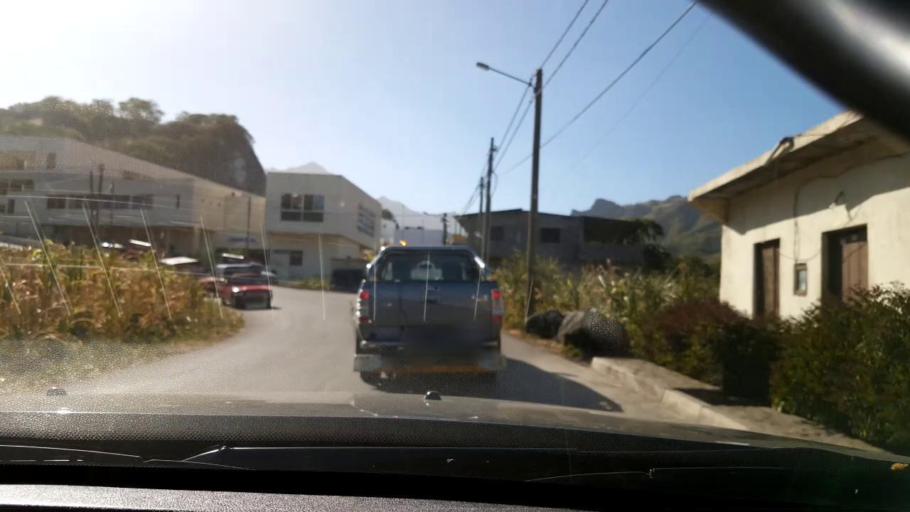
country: CV
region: Sao Lourenco dos Orgaos
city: Joao Teves
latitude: 15.0683
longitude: -23.5799
